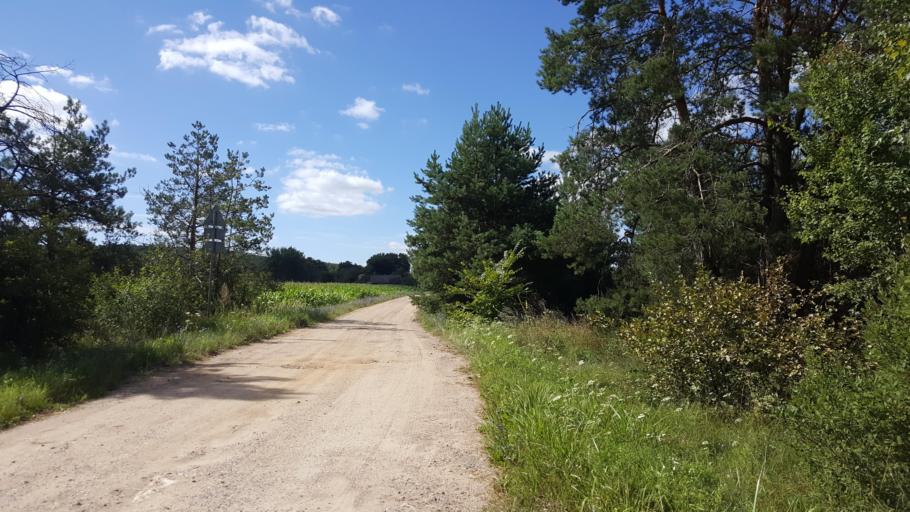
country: BY
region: Brest
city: Zhabinka
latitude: 52.3980
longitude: 24.0371
